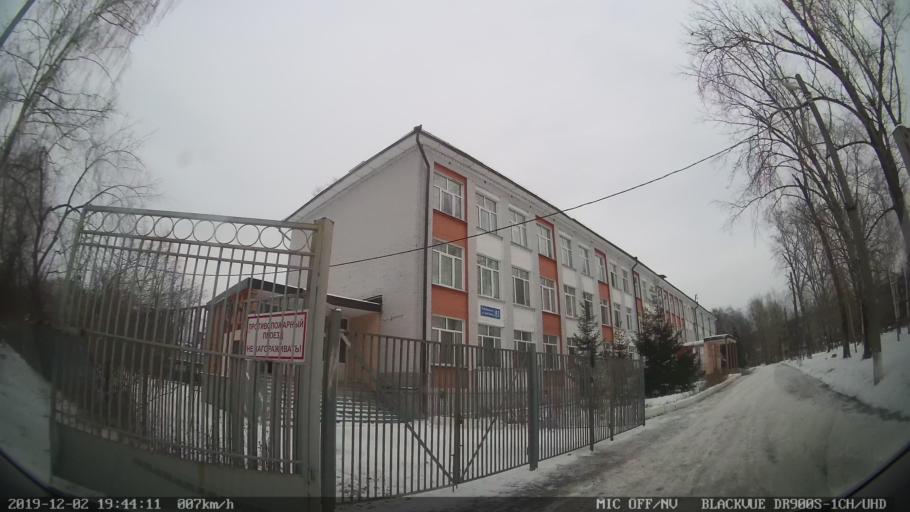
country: RU
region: Tatarstan
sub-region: Gorod Kazan'
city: Kazan
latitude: 55.7733
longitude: 49.1324
